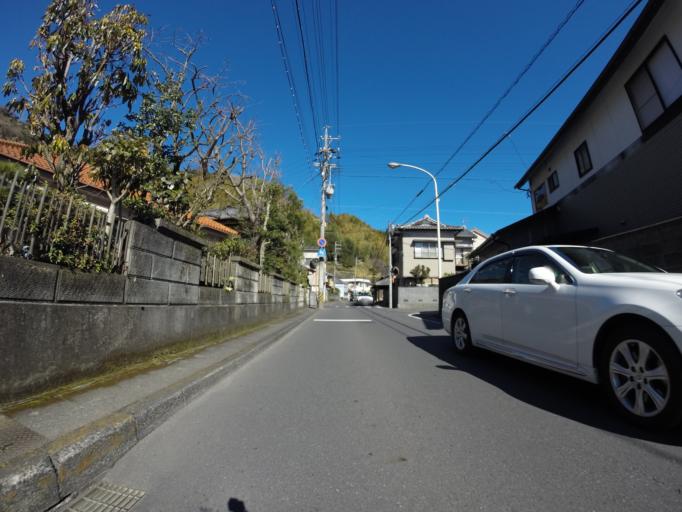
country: JP
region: Shizuoka
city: Shizuoka-shi
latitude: 35.0131
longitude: 138.3843
